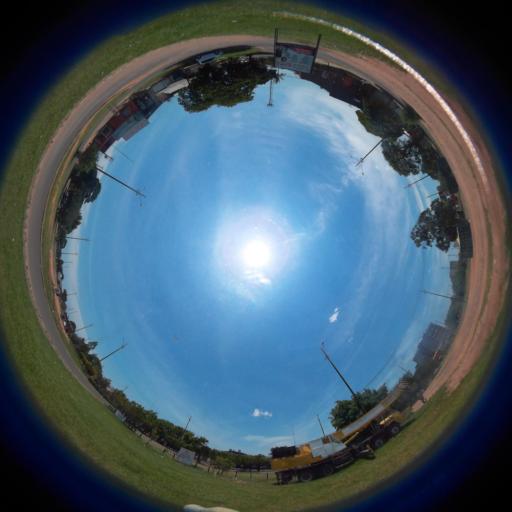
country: PY
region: Amambay
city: Pedro Juan Caballero
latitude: -22.5469
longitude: -55.7260
